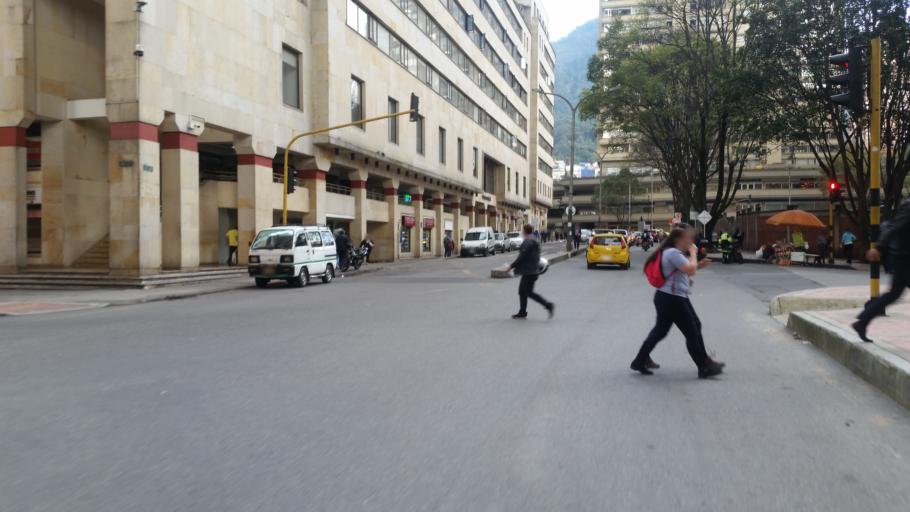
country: CO
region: Bogota D.C.
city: Bogota
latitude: 4.6161
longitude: -74.0711
